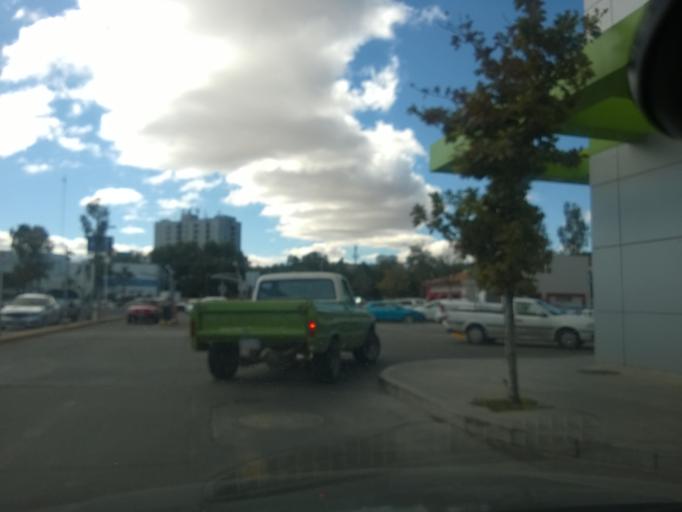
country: MX
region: Guanajuato
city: Leon
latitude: 21.1556
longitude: -101.6961
